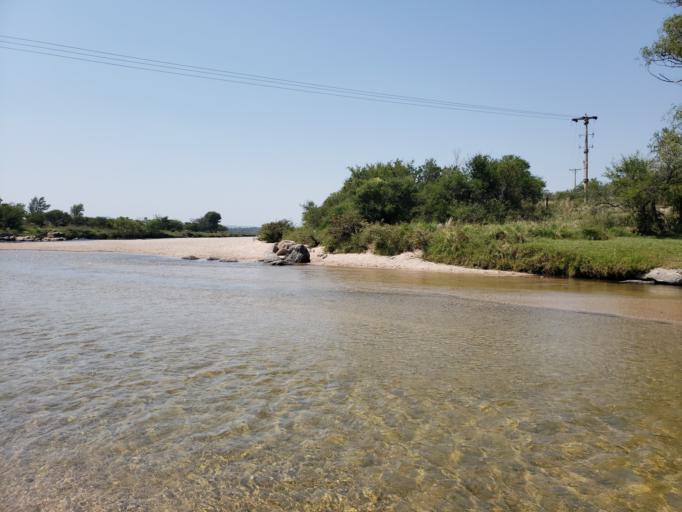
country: AR
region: Cordoba
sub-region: Departamento de Calamuchita
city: Villa Rumipal
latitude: -32.2621
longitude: -64.5122
